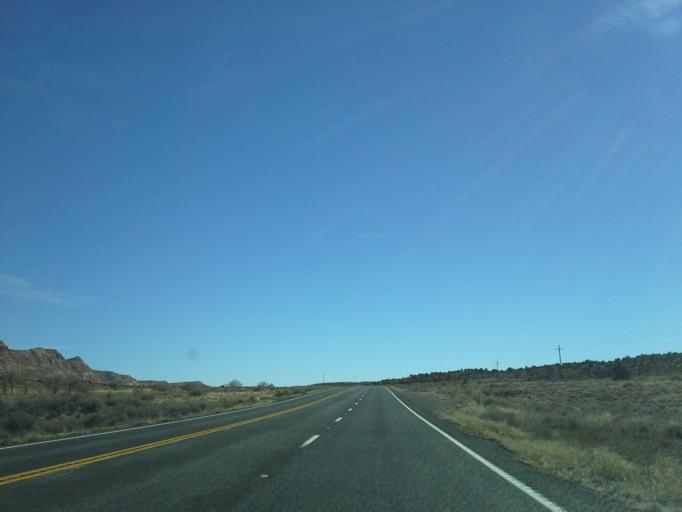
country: US
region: Arizona
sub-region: Coconino County
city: Tuba City
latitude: 36.4142
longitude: -111.5403
